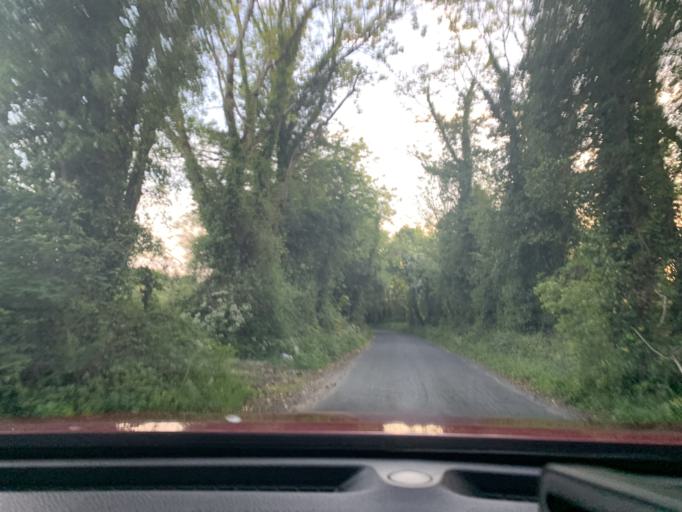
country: IE
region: Connaught
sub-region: Sligo
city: Sligo
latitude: 54.2907
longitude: -8.4571
